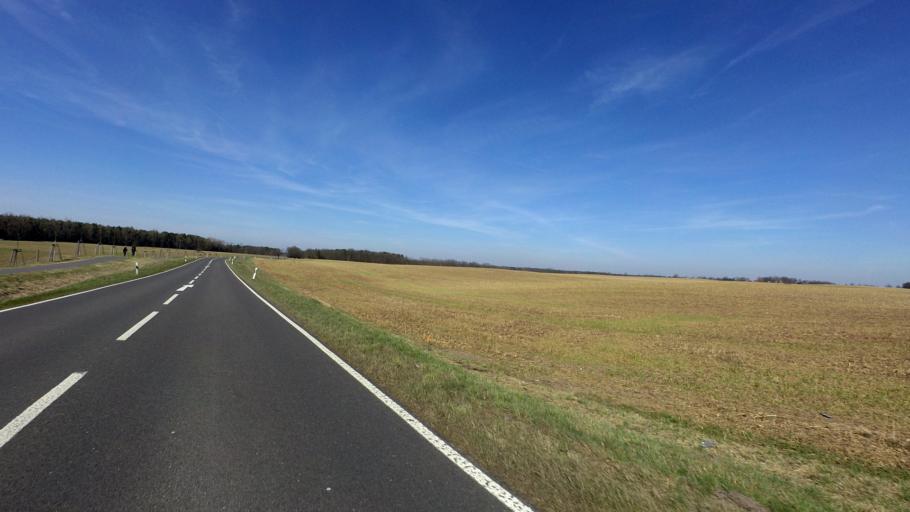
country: DE
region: Brandenburg
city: Furstenwalde
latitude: 52.3928
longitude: 14.0477
